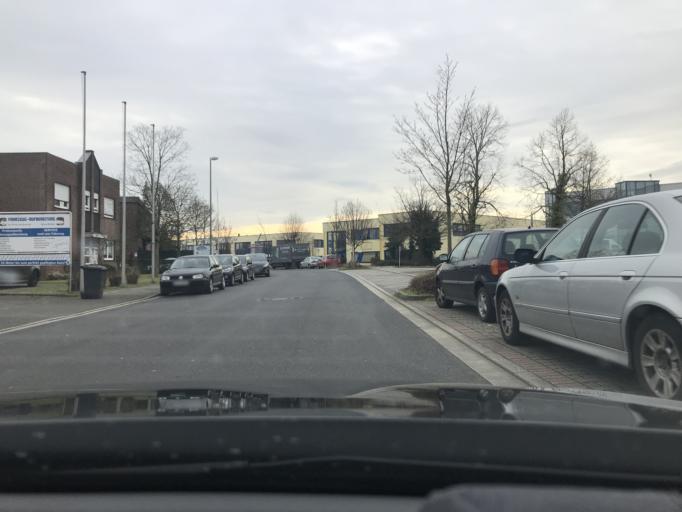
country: DE
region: North Rhine-Westphalia
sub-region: Regierungsbezirk Dusseldorf
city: Dusseldorf
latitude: 51.1688
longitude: 6.7469
